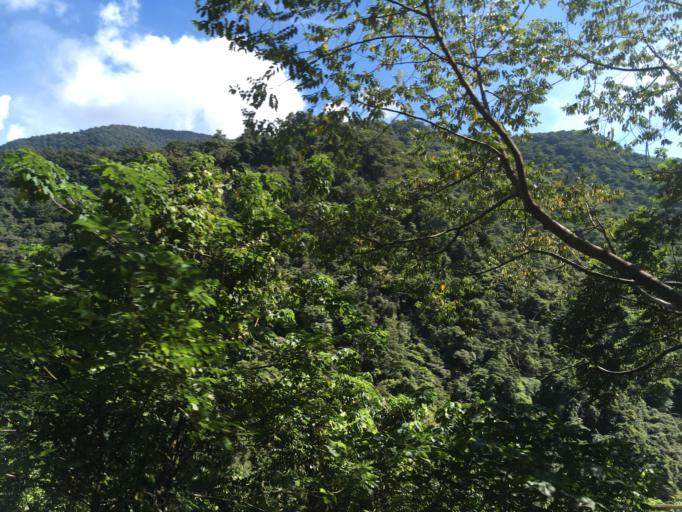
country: TW
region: Taiwan
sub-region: Yilan
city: Yilan
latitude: 24.4216
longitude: 121.7241
